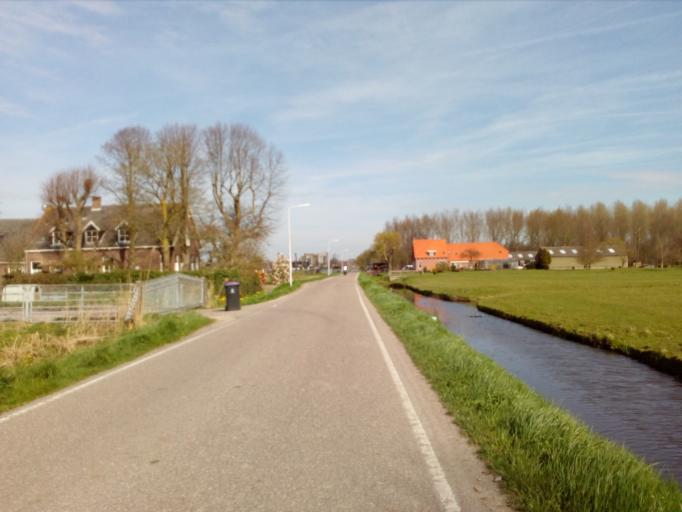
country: NL
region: South Holland
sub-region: Gemeente Delft
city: Delft
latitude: 51.9736
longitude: 4.3581
